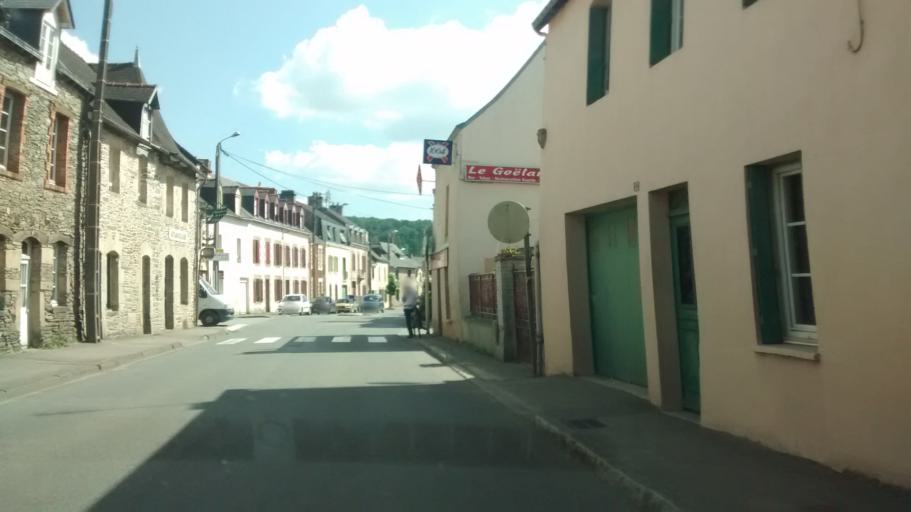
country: FR
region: Brittany
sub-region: Departement du Morbihan
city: Malestroit
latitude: 47.8113
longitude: -2.3779
